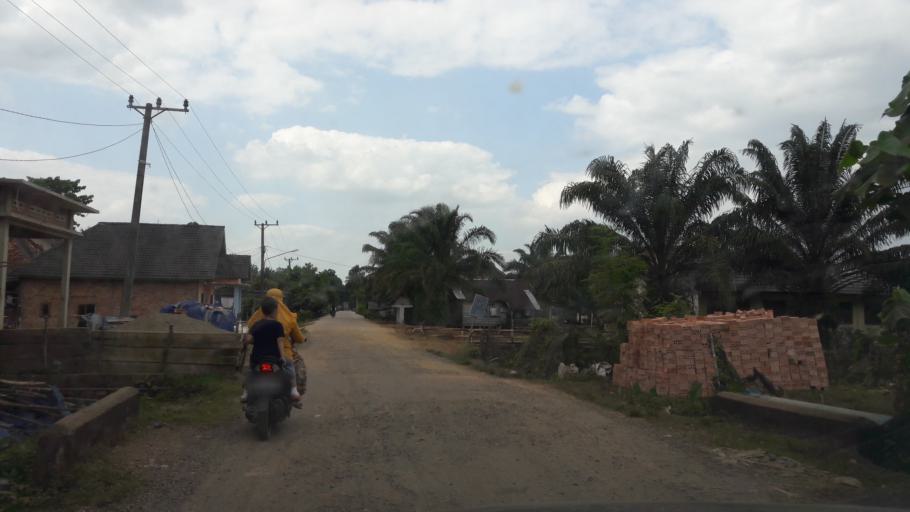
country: ID
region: South Sumatra
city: Prabumulih
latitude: -3.3369
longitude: 104.1073
